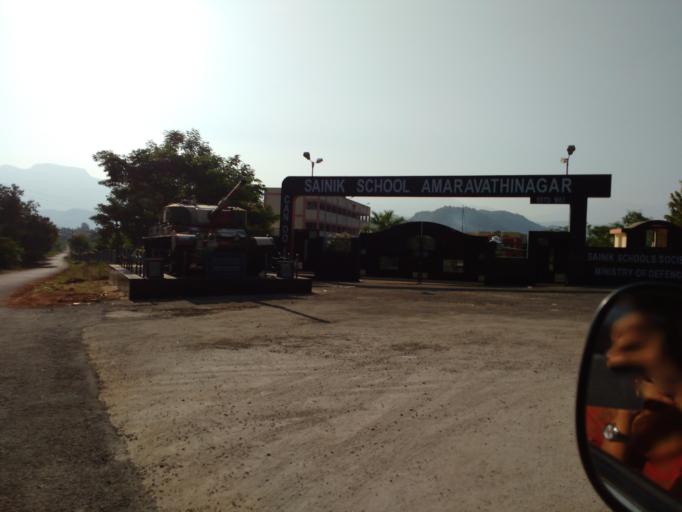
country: IN
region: Tamil Nadu
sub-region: Tiruppur
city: Kumaralingam
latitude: 10.4324
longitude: 77.2620
